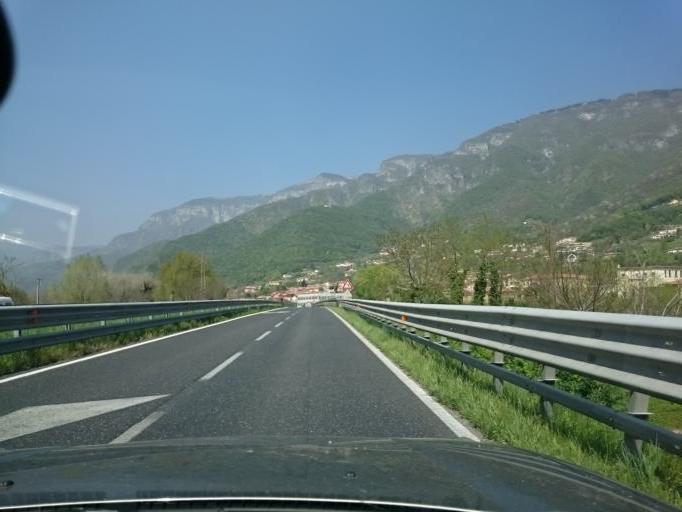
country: IT
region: Veneto
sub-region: Provincia di Vicenza
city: Solagna
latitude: 45.8148
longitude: 11.7167
